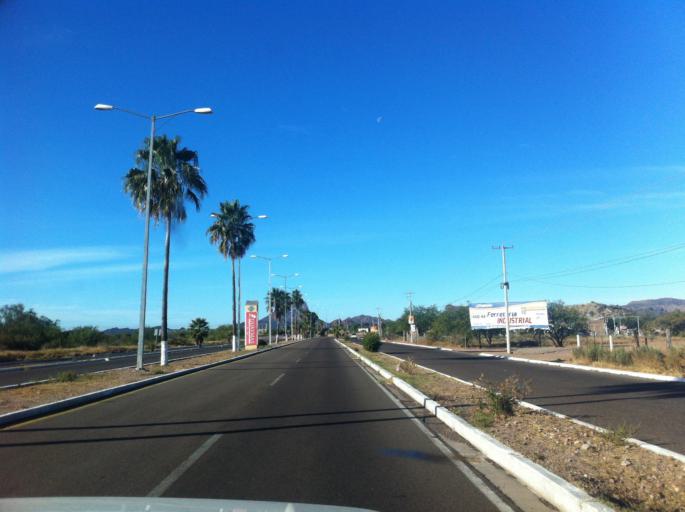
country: MX
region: Sonora
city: Heroica Guaymas
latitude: 27.9699
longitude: -111.0014
